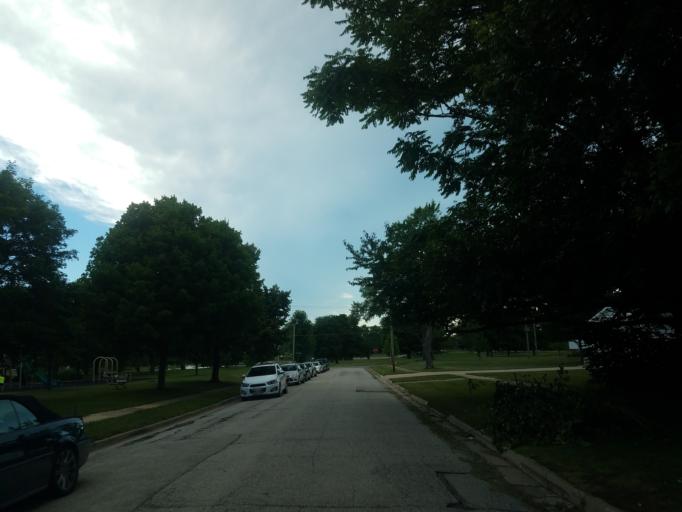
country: US
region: Illinois
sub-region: McLean County
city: Bloomington
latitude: 40.4695
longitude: -88.9712
